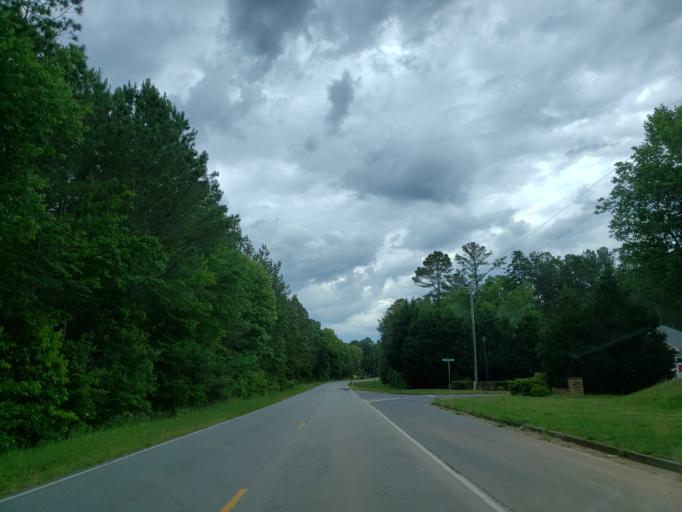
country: US
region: Georgia
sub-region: Polk County
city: Rockmart
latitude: 33.9431
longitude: -85.0450
